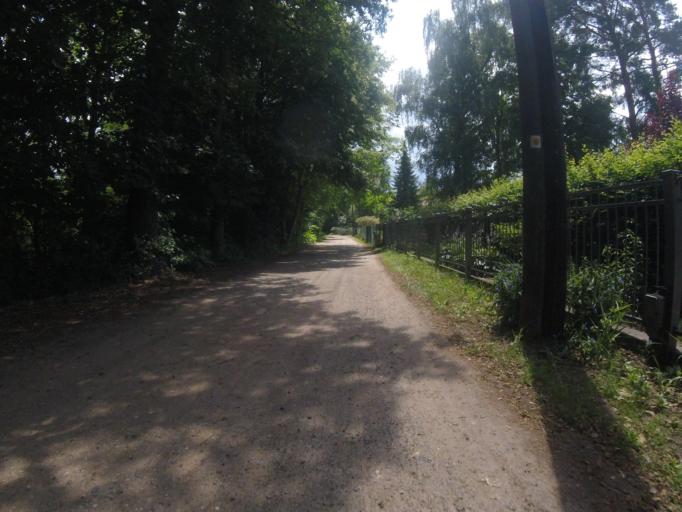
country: DE
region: Brandenburg
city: Bestensee
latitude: 52.2602
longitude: 13.6463
